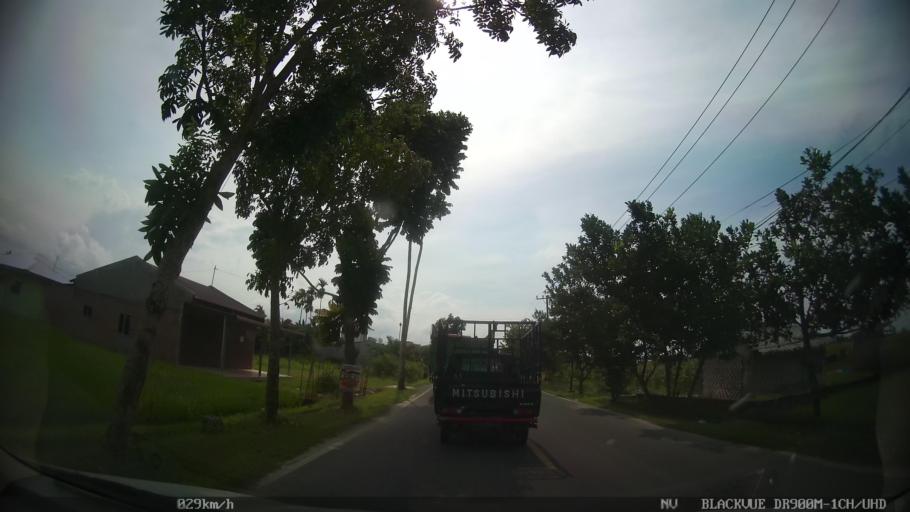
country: ID
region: North Sumatra
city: Percut
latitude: 3.6111
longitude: 98.8290
